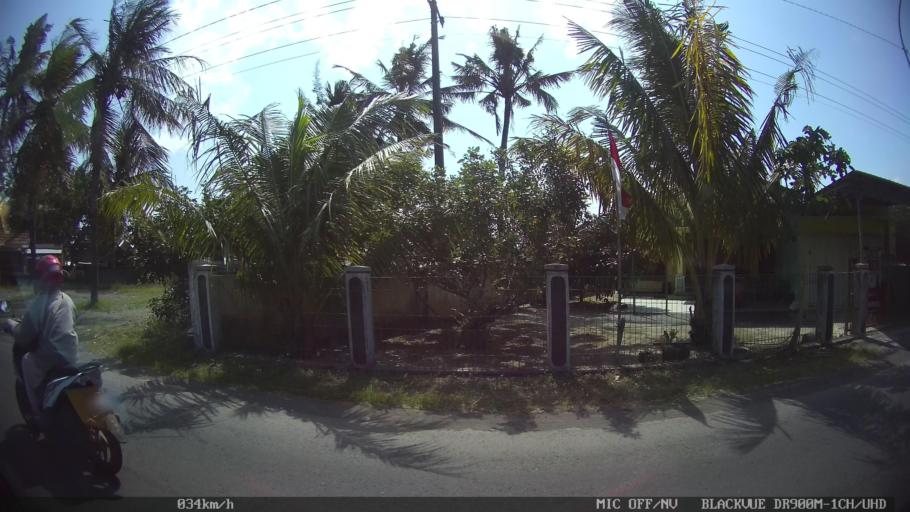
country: ID
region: Daerah Istimewa Yogyakarta
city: Pundong
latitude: -7.9778
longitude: 110.3402
